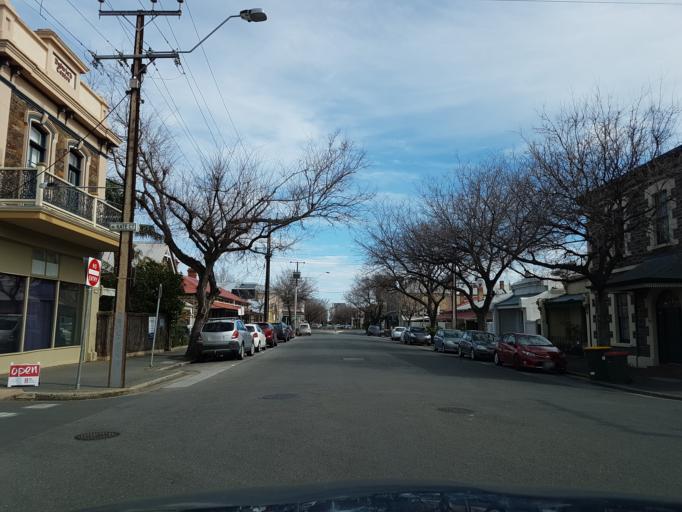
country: AU
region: South Australia
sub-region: Adelaide
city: Adelaide
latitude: -34.9309
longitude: 138.6137
